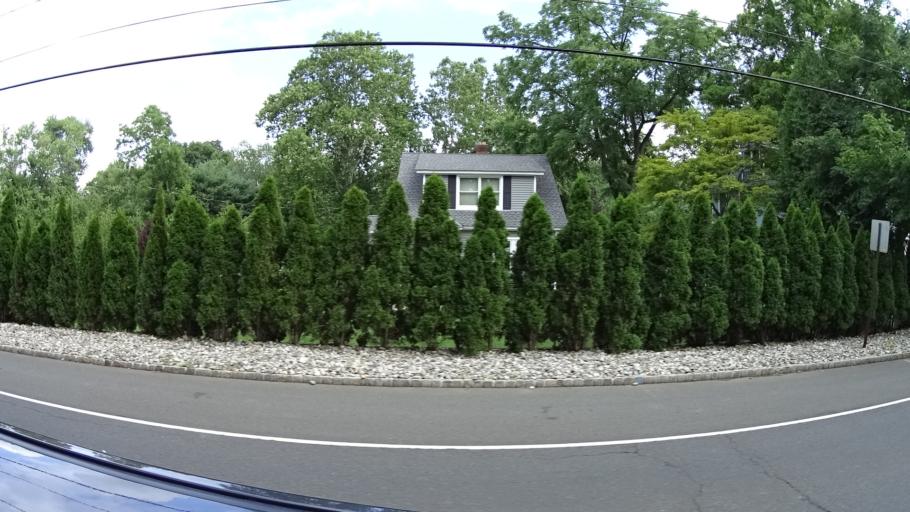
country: US
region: New Jersey
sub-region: Union County
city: New Providence
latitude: 40.6996
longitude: -74.4190
